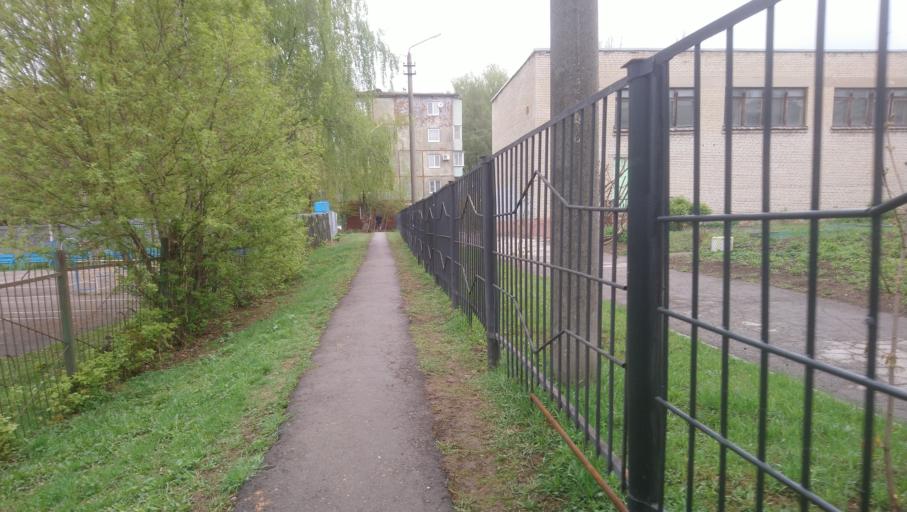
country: RU
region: Tula
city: Tula
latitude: 54.1942
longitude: 37.6737
